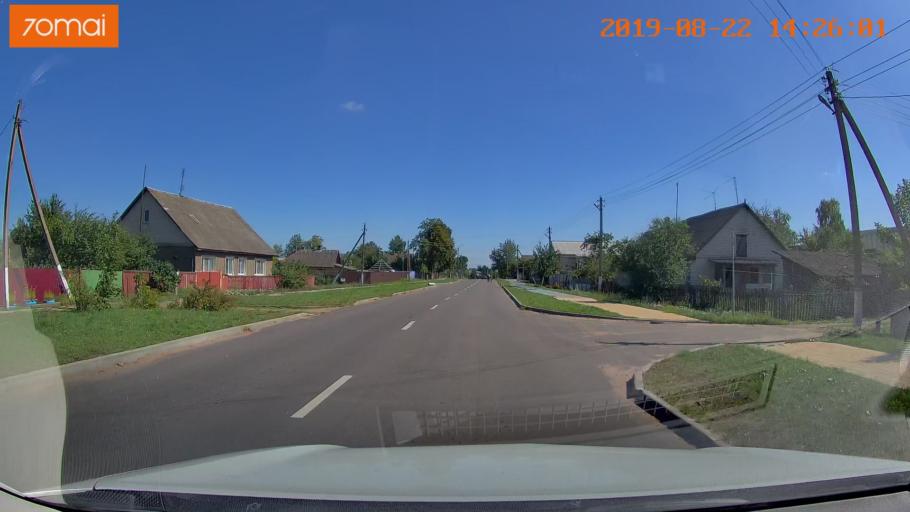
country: BY
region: Mogilev
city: Asipovichy
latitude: 53.3001
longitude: 28.6129
